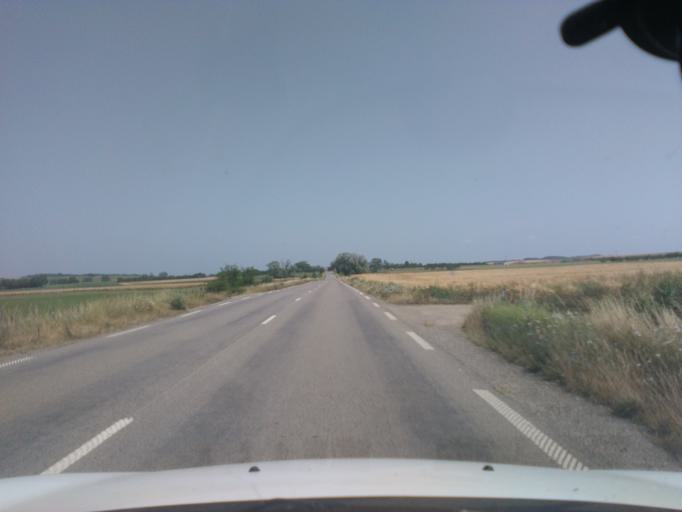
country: FR
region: Lorraine
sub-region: Departement des Vosges
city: Vittel
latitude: 48.3098
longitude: 5.9586
